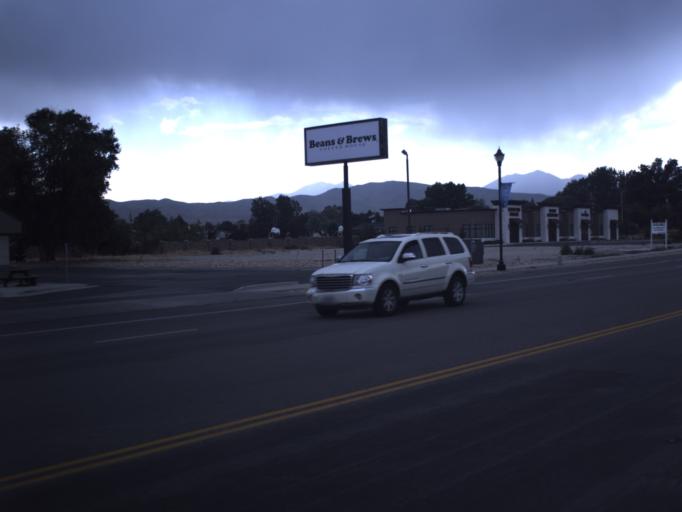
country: US
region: Utah
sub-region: Salt Lake County
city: Riverton
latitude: 40.5224
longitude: -111.9333
